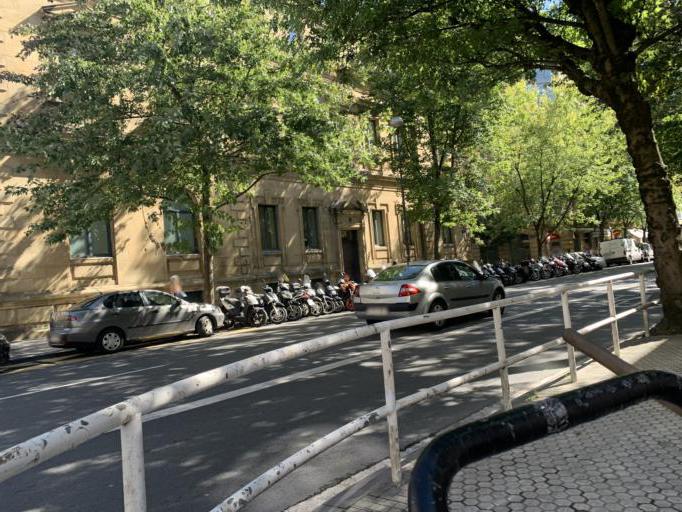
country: ES
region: Basque Country
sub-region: Provincia de Guipuzcoa
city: San Sebastian
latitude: 43.3161
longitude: -1.9820
